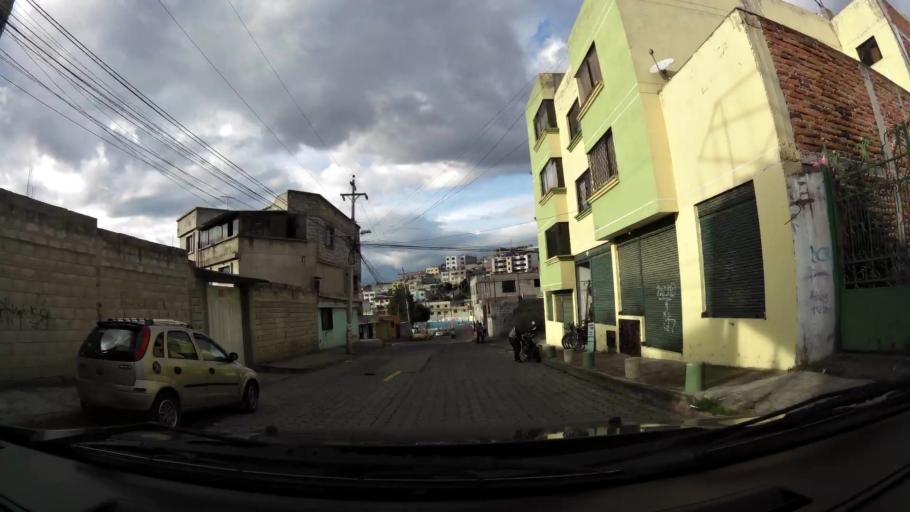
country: EC
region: Pichincha
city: Quito
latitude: -0.1291
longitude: -78.4631
